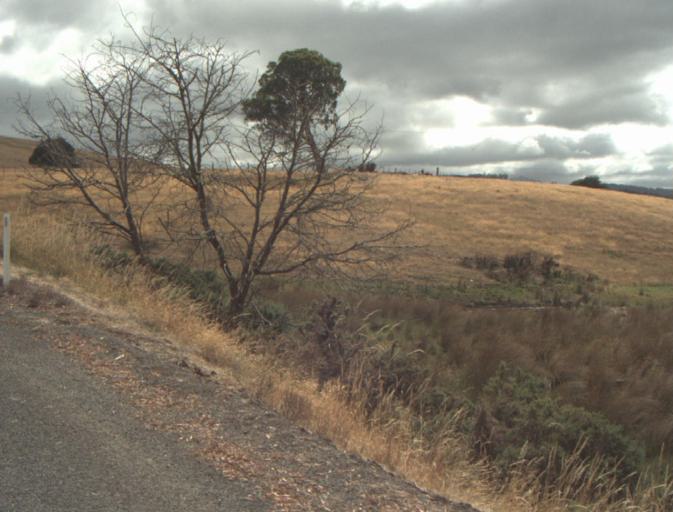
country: AU
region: Tasmania
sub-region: Northern Midlands
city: Evandale
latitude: -41.4786
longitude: 147.5004
